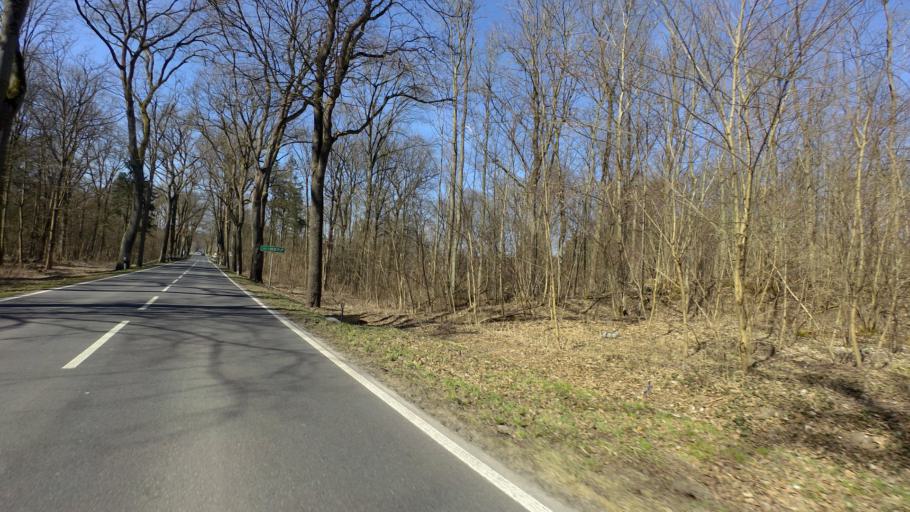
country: DE
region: Brandenburg
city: Waldsieversdorf
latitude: 52.5383
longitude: 14.0593
